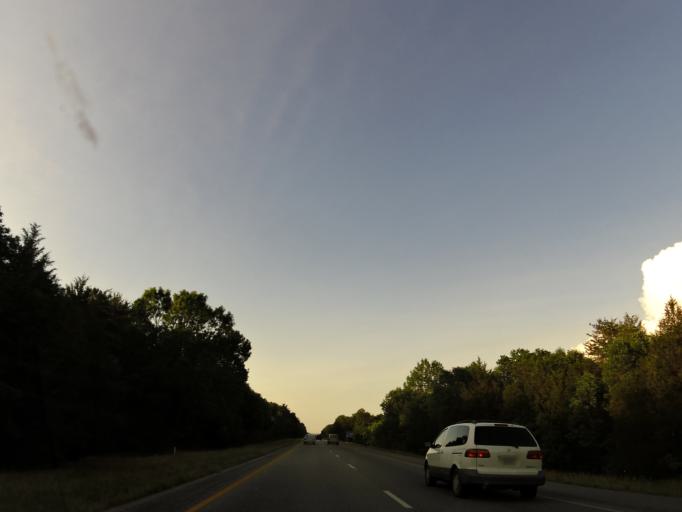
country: US
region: Georgia
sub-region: Dade County
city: Trenton
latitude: 34.8423
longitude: -85.5314
